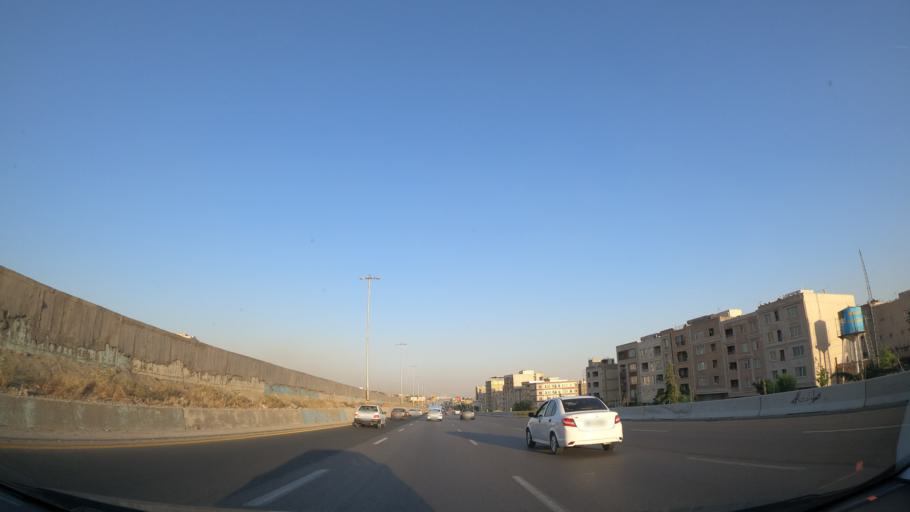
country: IR
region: Tehran
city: Shahr-e Qods
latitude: 35.7586
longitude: 51.0679
